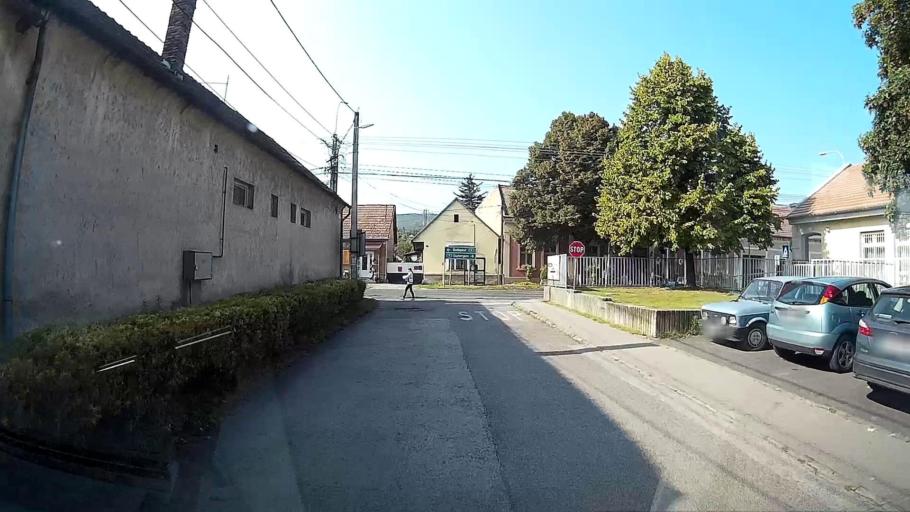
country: HU
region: Pest
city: Dunabogdany
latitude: 47.7945
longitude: 19.0355
